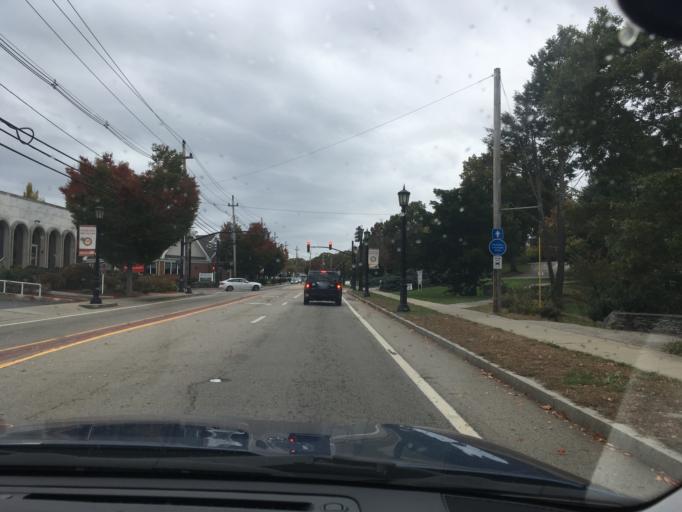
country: US
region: Rhode Island
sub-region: Bristol County
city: Barrington
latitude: 41.7394
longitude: -71.3073
